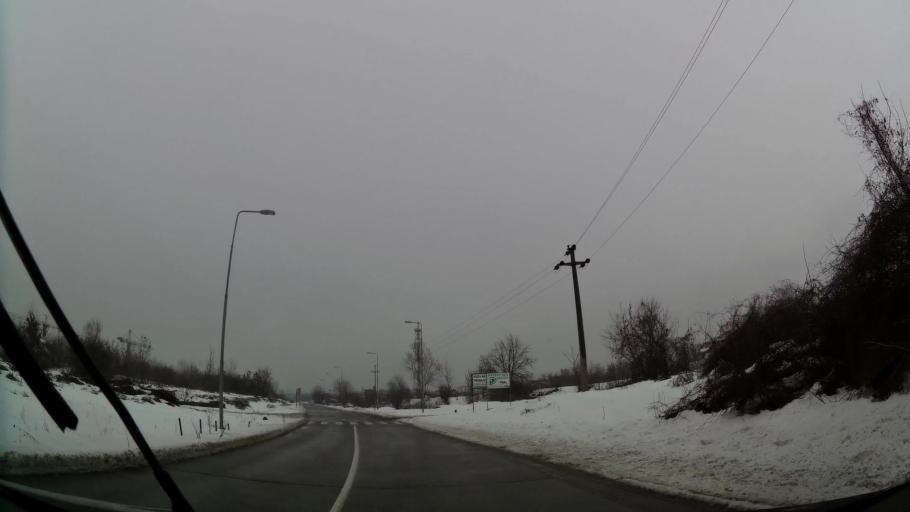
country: RS
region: Central Serbia
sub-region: Belgrade
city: Zemun
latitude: 44.8404
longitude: 20.3522
